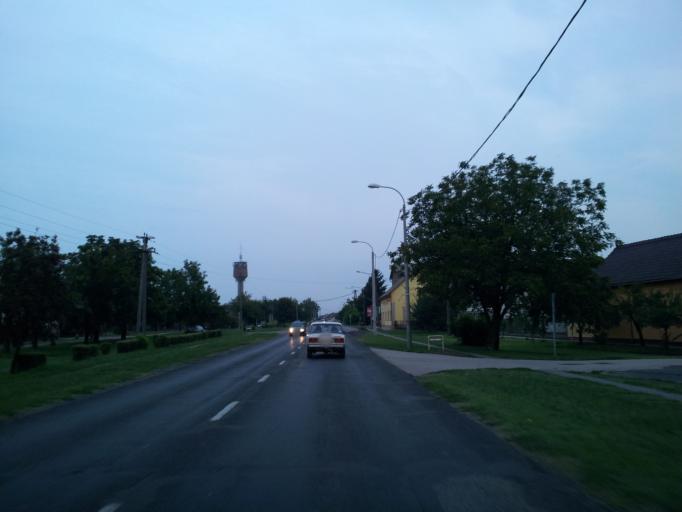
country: HU
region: Tolna
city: Tolna
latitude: 46.4193
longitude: 18.7674
